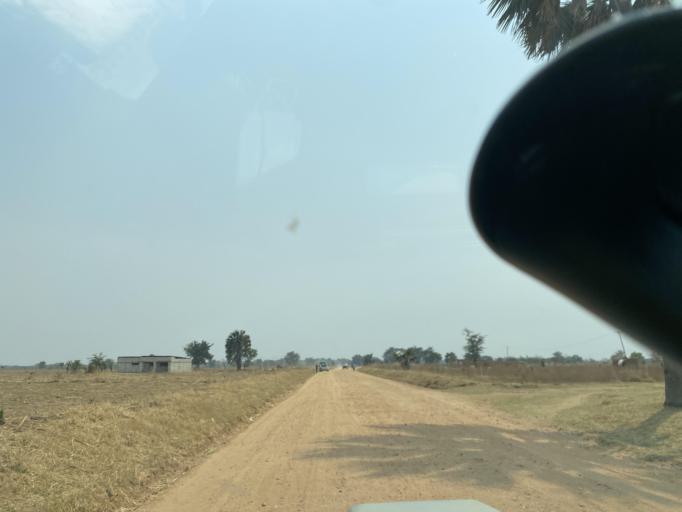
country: ZM
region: Lusaka
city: Kafue
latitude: -15.6373
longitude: 28.0983
